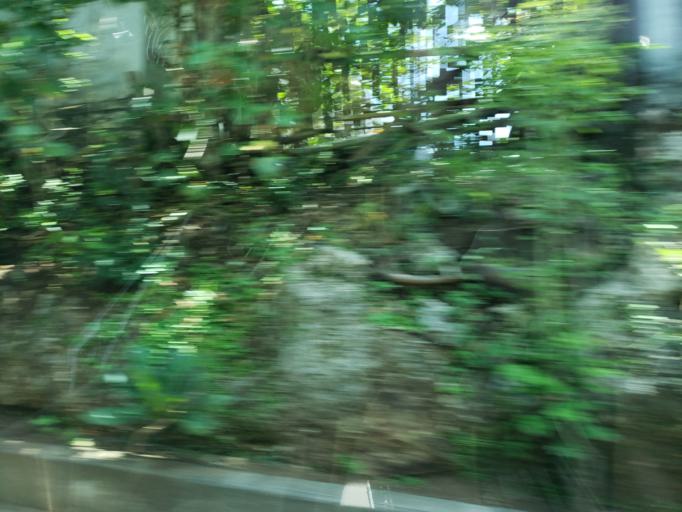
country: ID
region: Bali
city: Pecatu
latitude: -8.8417
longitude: 115.1223
